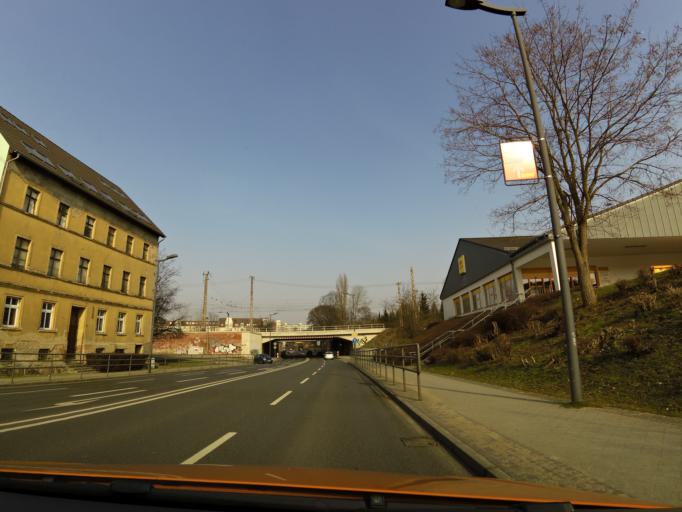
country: DE
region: Brandenburg
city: Frankfurt (Oder)
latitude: 52.3386
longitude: 14.5397
